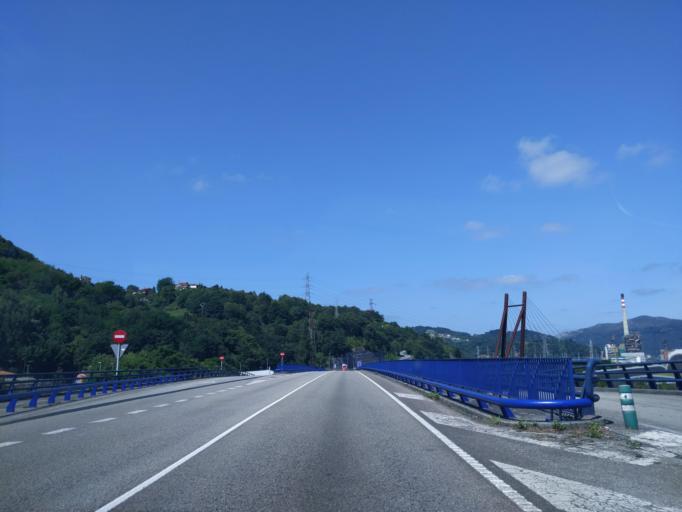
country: ES
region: Asturias
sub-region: Province of Asturias
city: Sama
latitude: 43.2991
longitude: -5.6867
